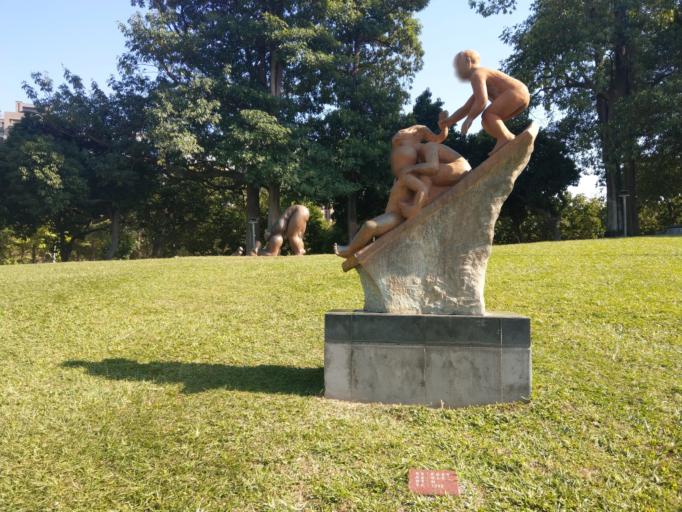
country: TW
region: Taiwan
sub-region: Taichung City
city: Taichung
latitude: 24.1304
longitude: 120.6434
